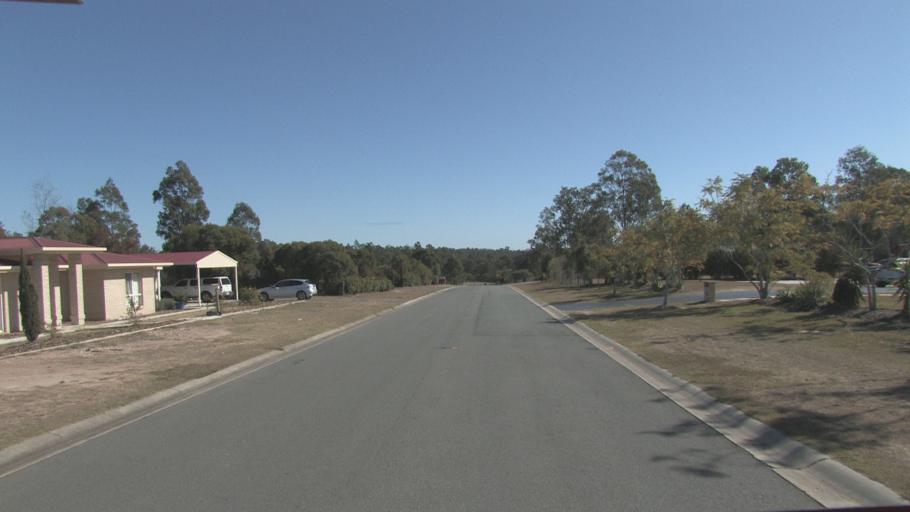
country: AU
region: Queensland
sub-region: Logan
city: Cedar Vale
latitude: -27.8583
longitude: 153.0444
